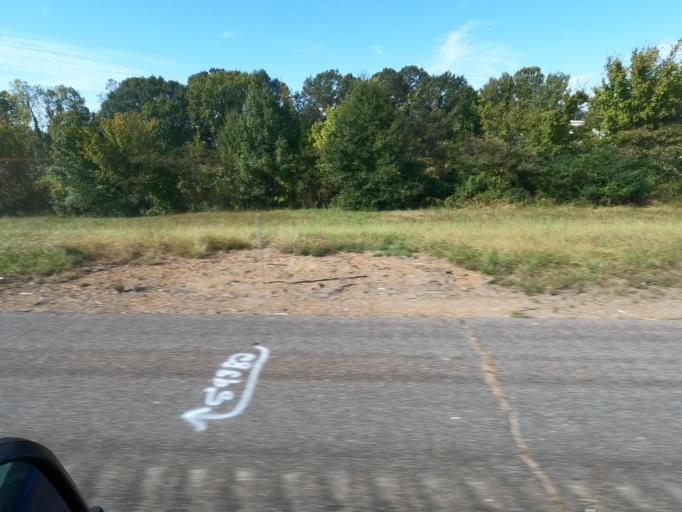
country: US
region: Tennessee
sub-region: Shelby County
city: Arlington
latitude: 35.2810
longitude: -89.6808
